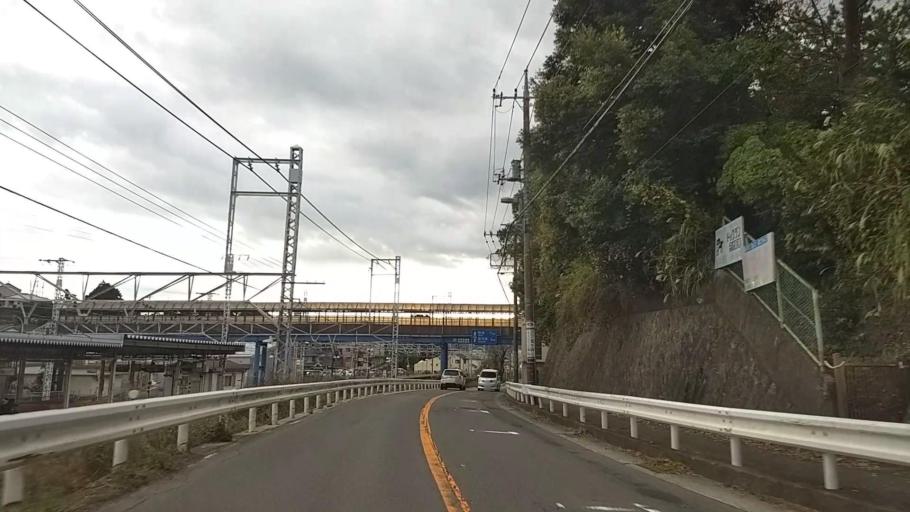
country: JP
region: Kanagawa
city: Yugawara
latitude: 35.1571
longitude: 139.1322
